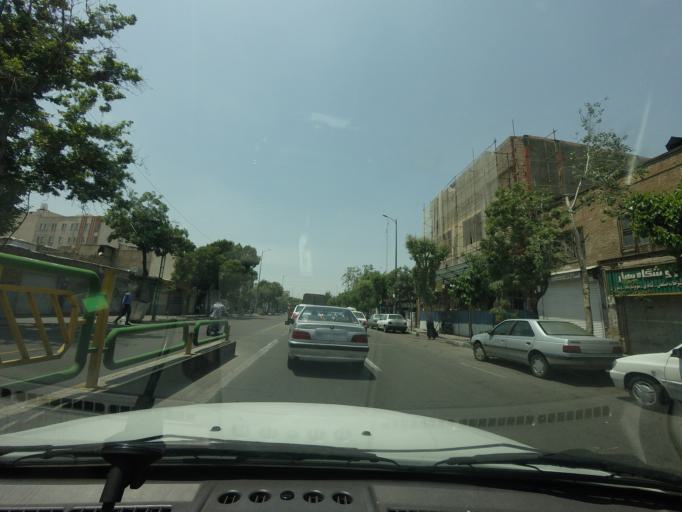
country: IR
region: Tehran
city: Tehran
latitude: 35.6696
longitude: 51.4330
